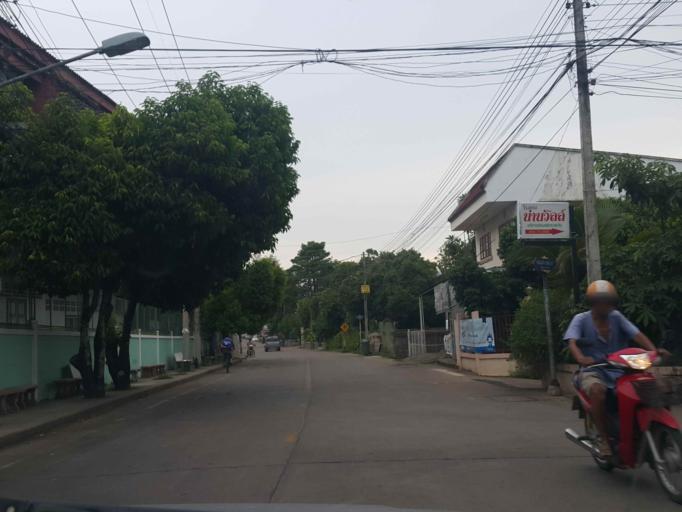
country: TH
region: Nan
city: Nan
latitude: 18.7782
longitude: 100.7806
